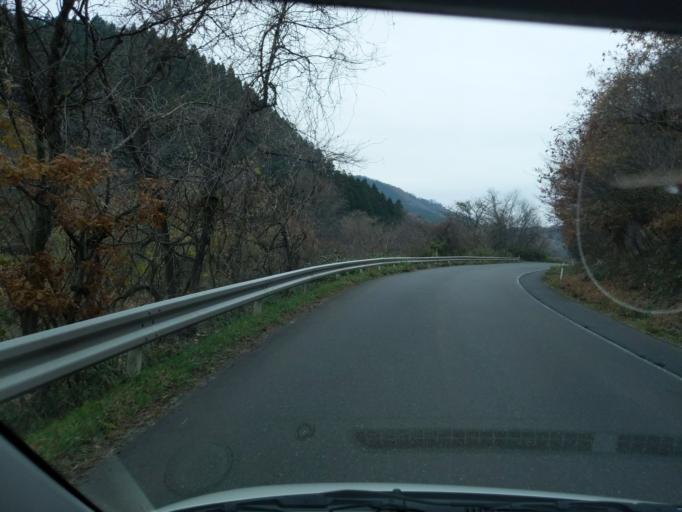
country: JP
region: Iwate
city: Kitakami
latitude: 39.2709
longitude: 141.1780
